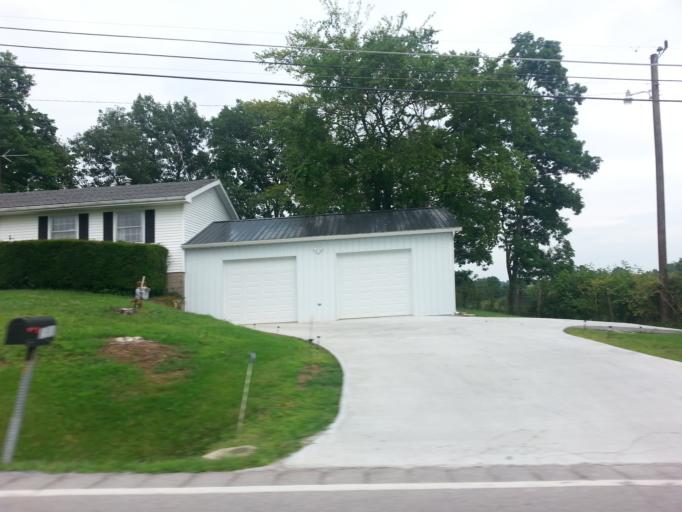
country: US
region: Kentucky
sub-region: Robertson County
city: Mount Olivet
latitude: 38.5297
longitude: -84.0594
